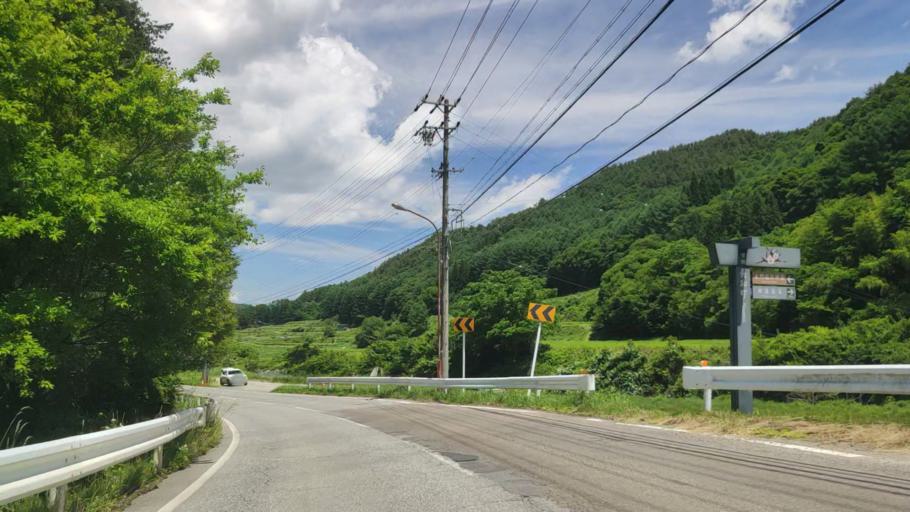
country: JP
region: Nagano
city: Kamimaruko
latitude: 36.1918
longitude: 138.2445
